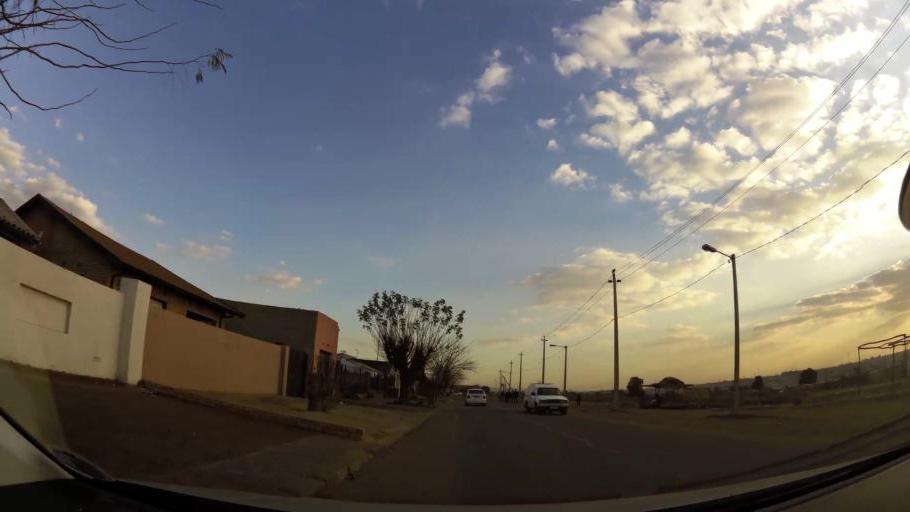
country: ZA
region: Gauteng
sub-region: City of Johannesburg Metropolitan Municipality
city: Soweto
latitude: -26.2663
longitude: 27.8954
